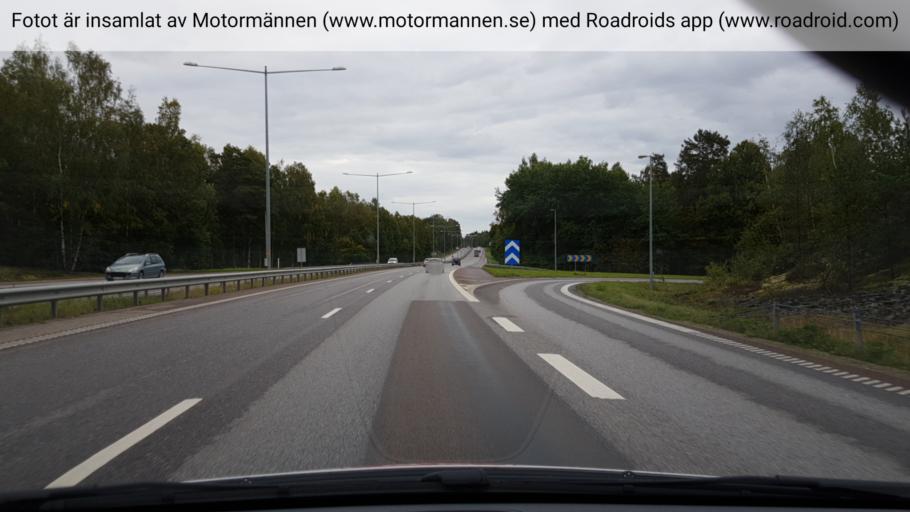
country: SE
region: Vaermland
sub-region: Karlstads Kommun
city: Karlstad
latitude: 59.4012
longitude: 13.5547
